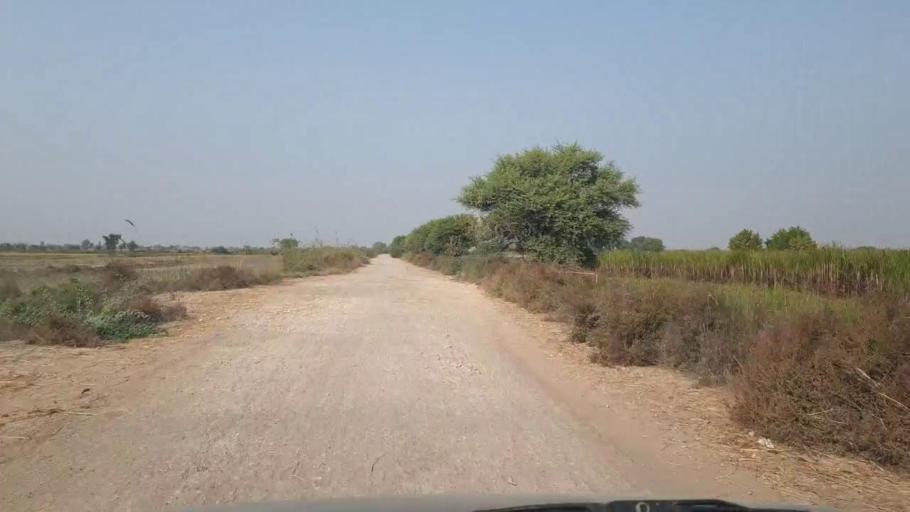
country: PK
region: Sindh
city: Tando Muhammad Khan
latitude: 25.0898
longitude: 68.3390
